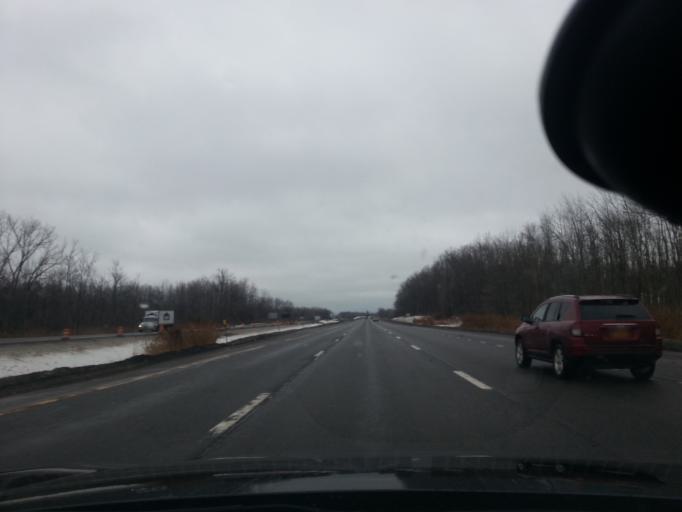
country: US
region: New York
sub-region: Onondaga County
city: Brewerton
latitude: 43.2286
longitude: -76.1289
